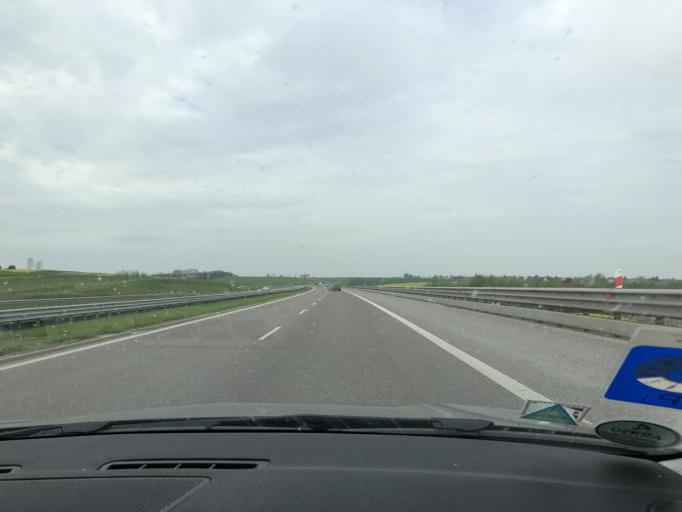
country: PL
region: Subcarpathian Voivodeship
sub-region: Powiat jaroslawski
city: Wierzbna
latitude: 50.0159
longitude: 22.5905
